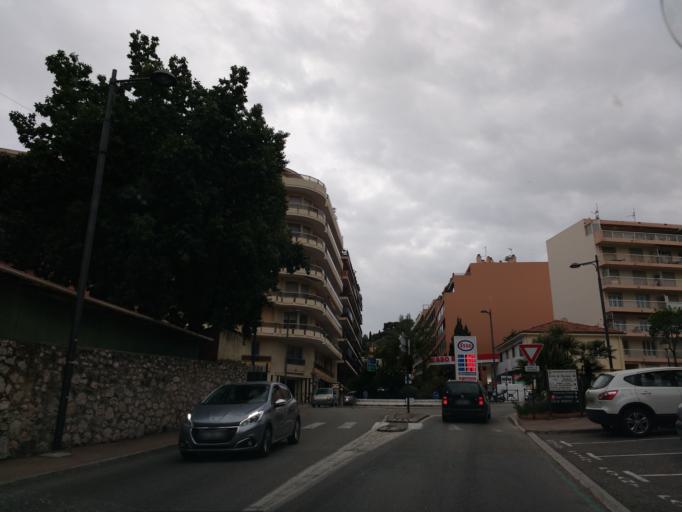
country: FR
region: Provence-Alpes-Cote d'Azur
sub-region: Departement des Alpes-Maritimes
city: Roquebrune-Cap-Martin
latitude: 43.7640
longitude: 7.4807
